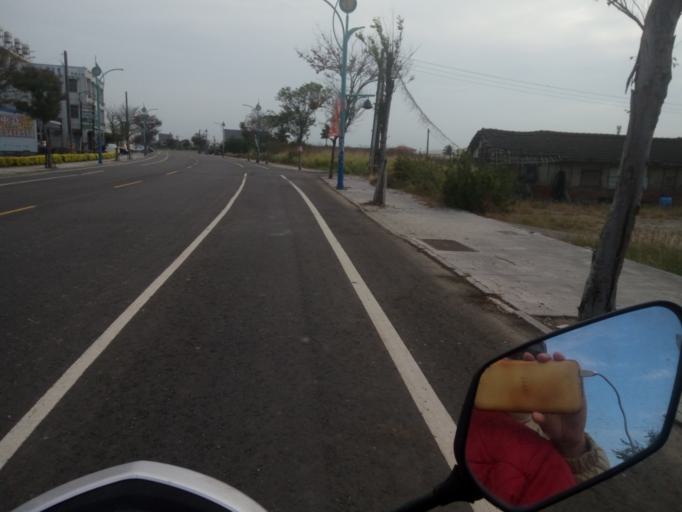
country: TW
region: Taiwan
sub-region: Chiayi
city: Taibao
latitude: 23.4806
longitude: 120.3350
